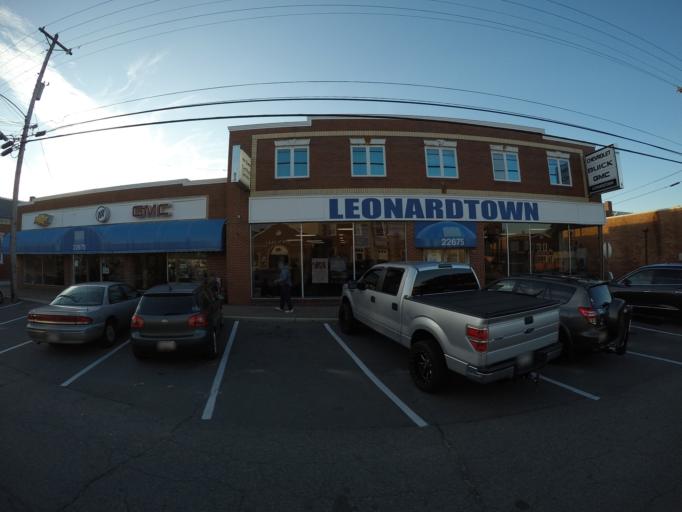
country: US
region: Maryland
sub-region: Saint Mary's County
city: Leonardtown
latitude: 38.2904
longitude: -76.6362
